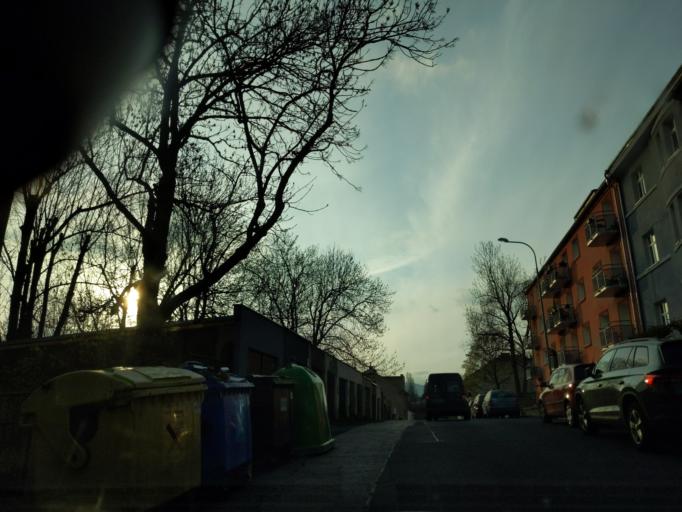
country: CZ
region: Ustecky
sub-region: Okres Usti nad Labem
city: Usti nad Labem
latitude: 50.6668
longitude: 14.0320
